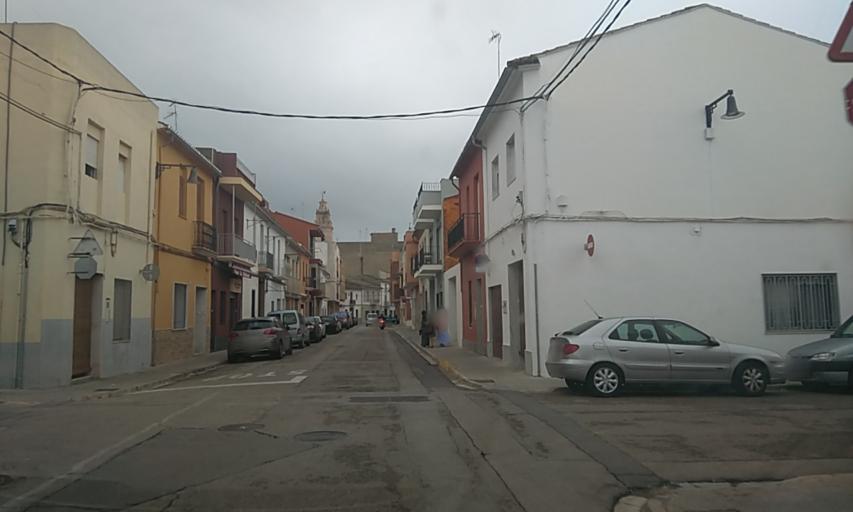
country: ES
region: Valencia
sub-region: Provincia de Valencia
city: L'Alcudia
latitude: 39.1980
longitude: -0.5086
